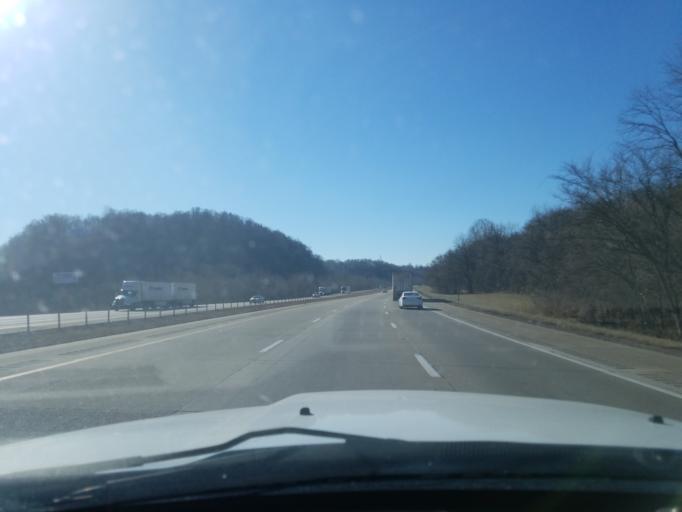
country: US
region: Kentucky
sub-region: Bullitt County
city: Lebanon Junction
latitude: 37.7787
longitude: -85.7748
